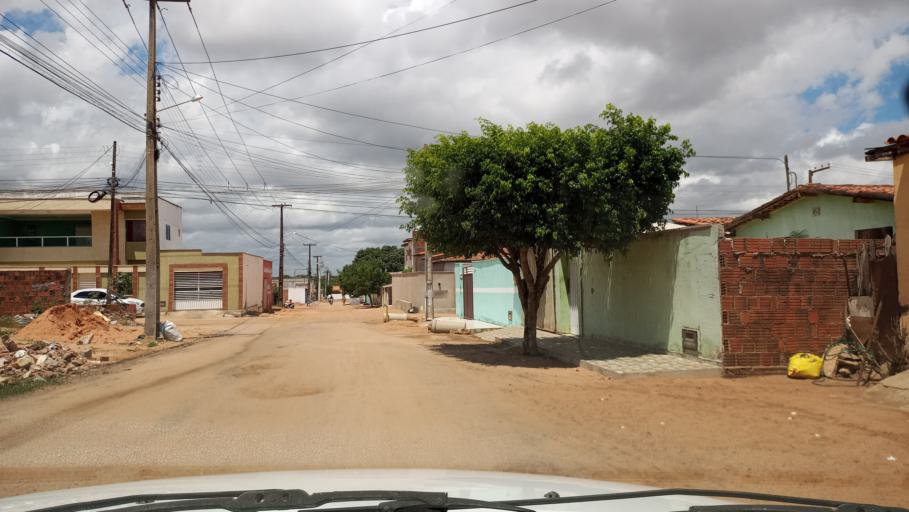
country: BR
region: Rio Grande do Norte
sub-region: Joao Camara
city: Joao Camara
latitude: -5.5281
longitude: -35.8091
